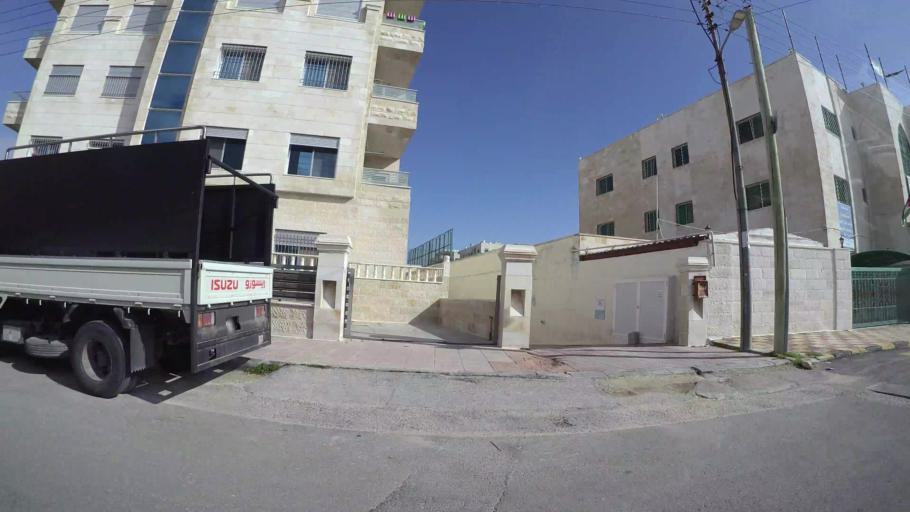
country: JO
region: Amman
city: Wadi as Sir
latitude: 31.9504
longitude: 35.8442
